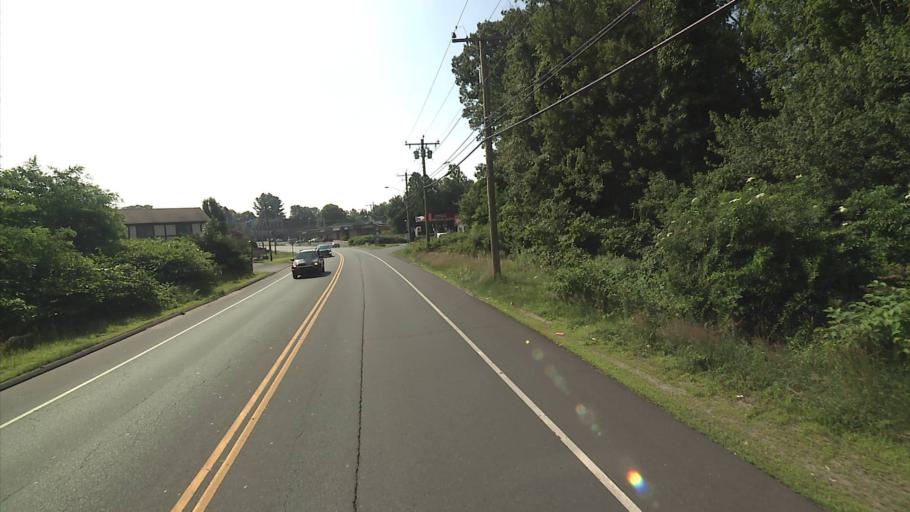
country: US
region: Connecticut
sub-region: New Haven County
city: Wolcott
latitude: 41.5529
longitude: -72.9886
